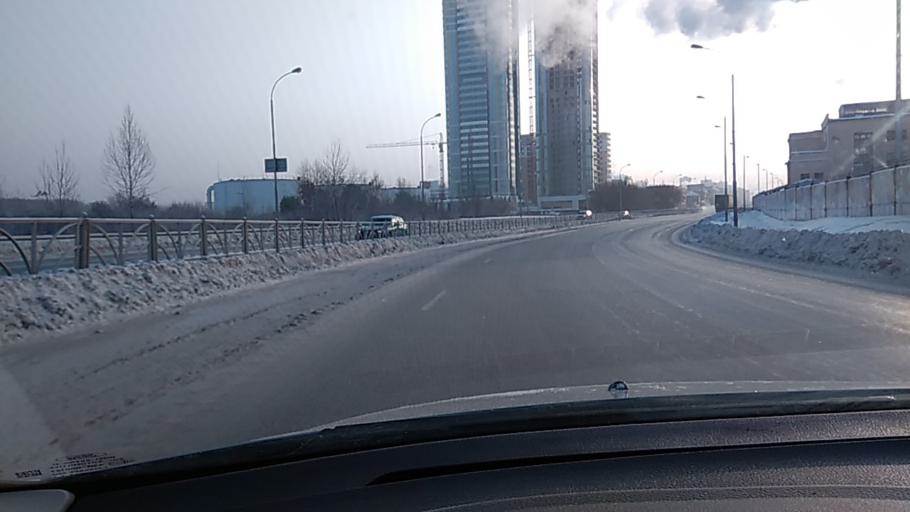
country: RU
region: Sverdlovsk
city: Yekaterinburg
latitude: 56.8163
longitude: 60.6278
